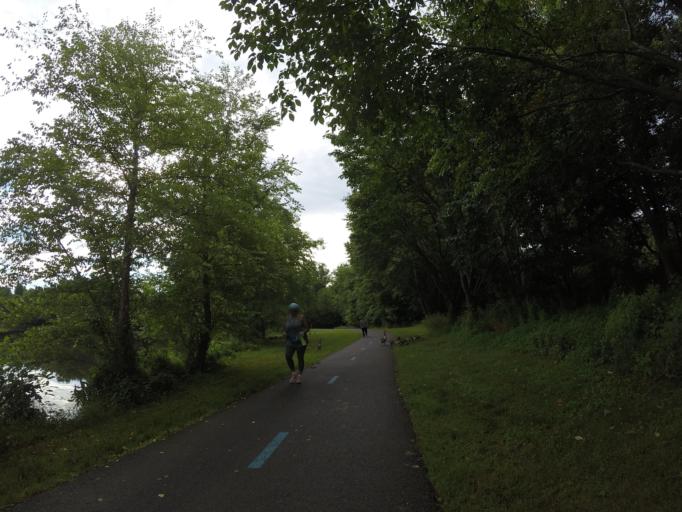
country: US
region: Maryland
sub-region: Prince George's County
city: Berwyn Heights
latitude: 38.9835
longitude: -76.9218
